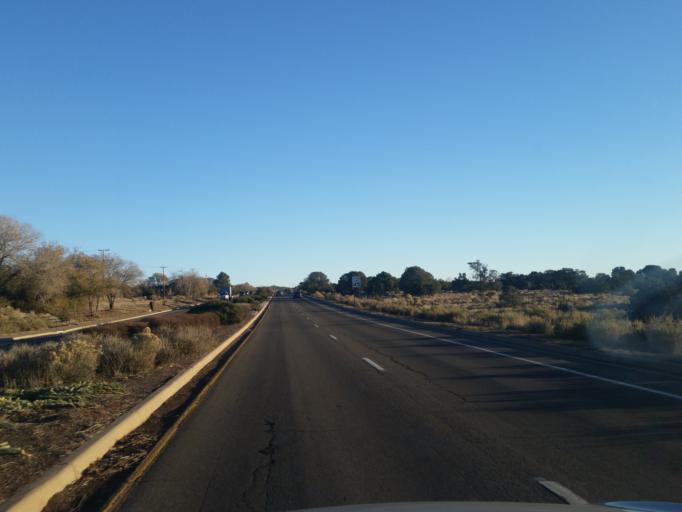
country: US
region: New Mexico
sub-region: Santa Fe County
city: Santa Fe
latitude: 35.6508
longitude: -105.9361
